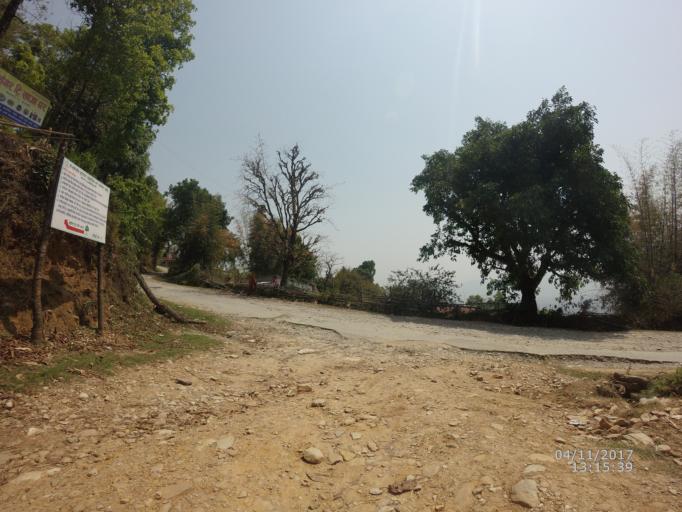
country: NP
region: Western Region
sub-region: Gandaki Zone
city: Pokhara
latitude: 28.2090
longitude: 84.0395
